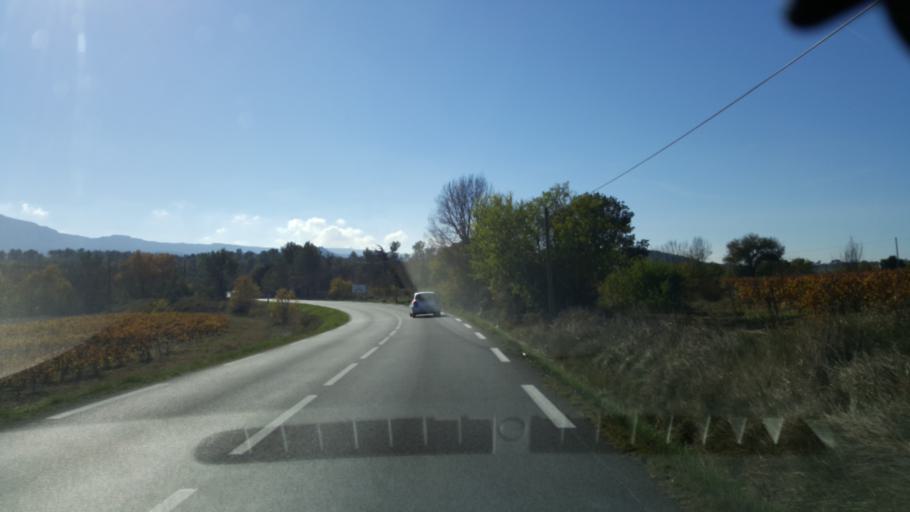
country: FR
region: Provence-Alpes-Cote d'Azur
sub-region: Departement du Var
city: Nans-les-Pins
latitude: 43.3967
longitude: 5.8012
